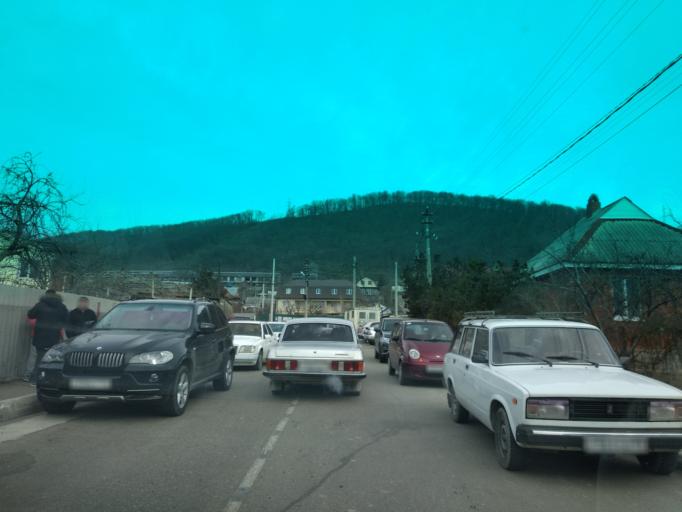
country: RU
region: Krasnodarskiy
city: Novomikhaylovskiy
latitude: 44.2506
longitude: 38.8389
